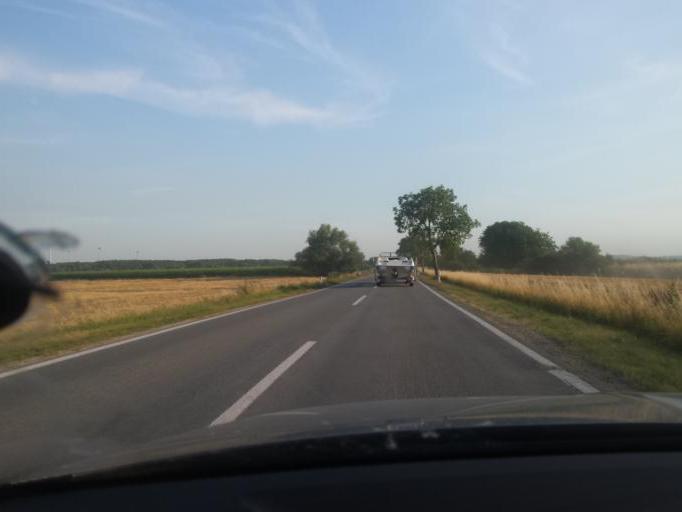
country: AT
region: Lower Austria
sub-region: Politischer Bezirk Bruck an der Leitha
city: Rohrau
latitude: 48.0796
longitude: 16.8626
